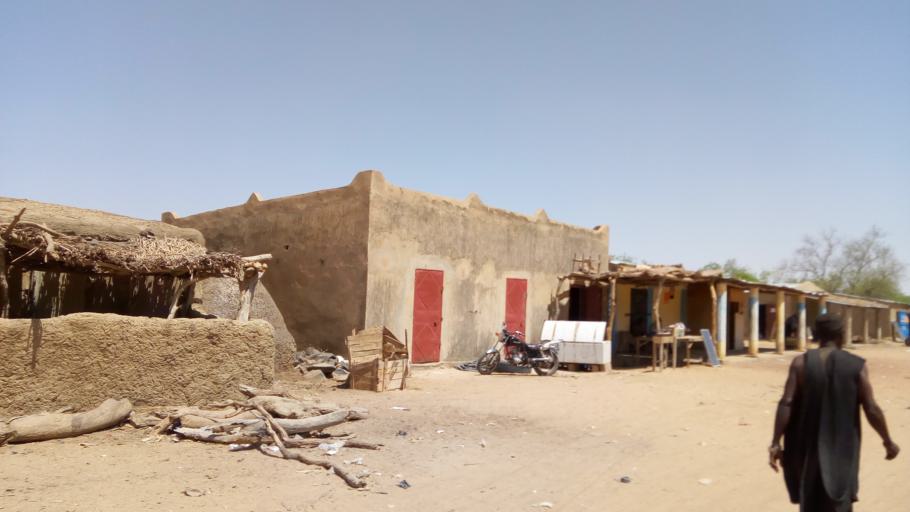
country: ML
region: Kayes
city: Diema
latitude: 14.5098
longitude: -8.8428
